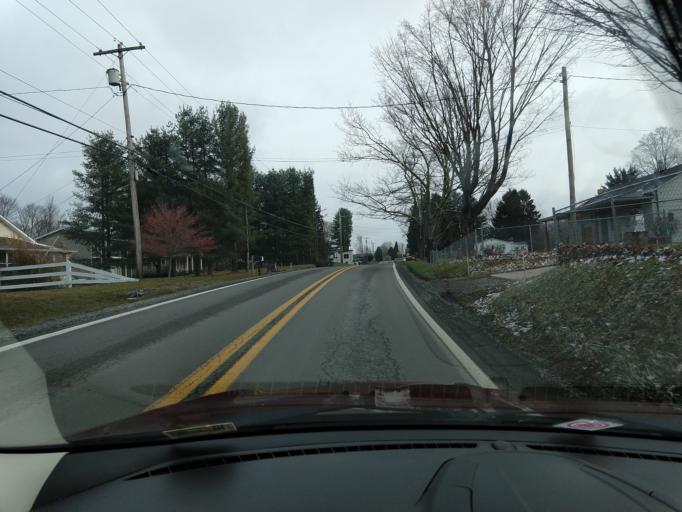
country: US
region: West Virginia
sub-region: Nicholas County
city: Craigsville
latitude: 38.2103
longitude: -80.6786
